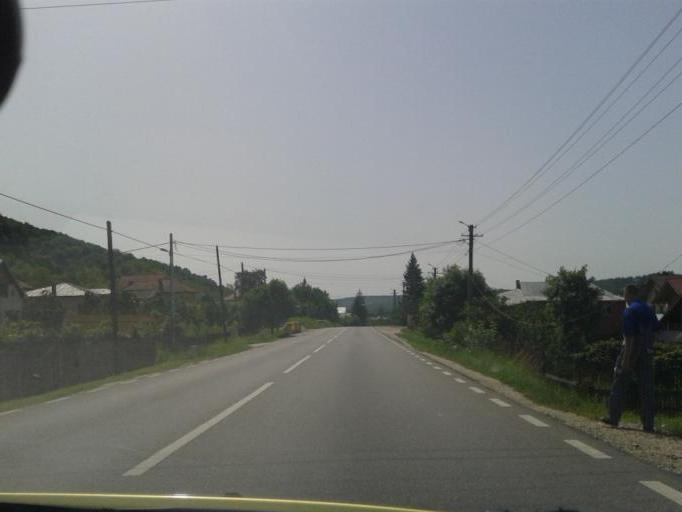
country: RO
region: Arges
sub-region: Comuna Babana
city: Babana
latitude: 44.9028
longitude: 24.7326
